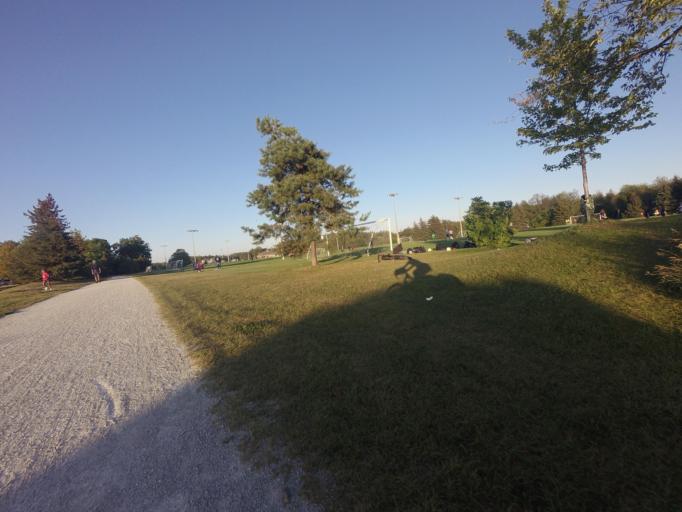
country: CA
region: Ontario
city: Brampton
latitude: 43.8743
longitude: -79.8580
